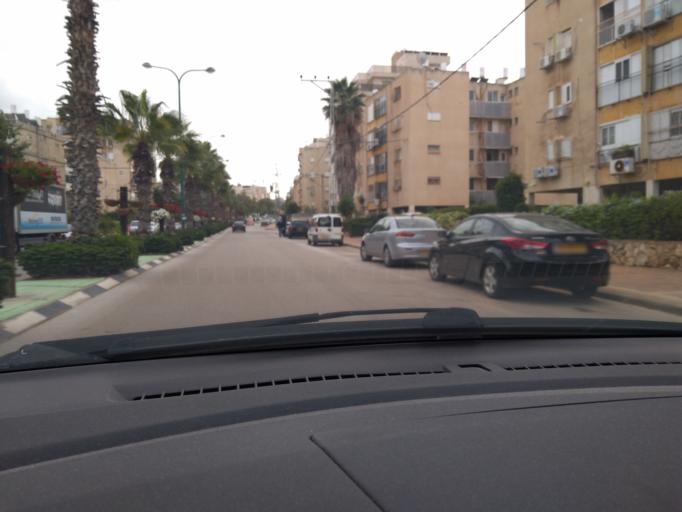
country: IL
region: Central District
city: Netanya
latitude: 32.3404
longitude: 34.8566
